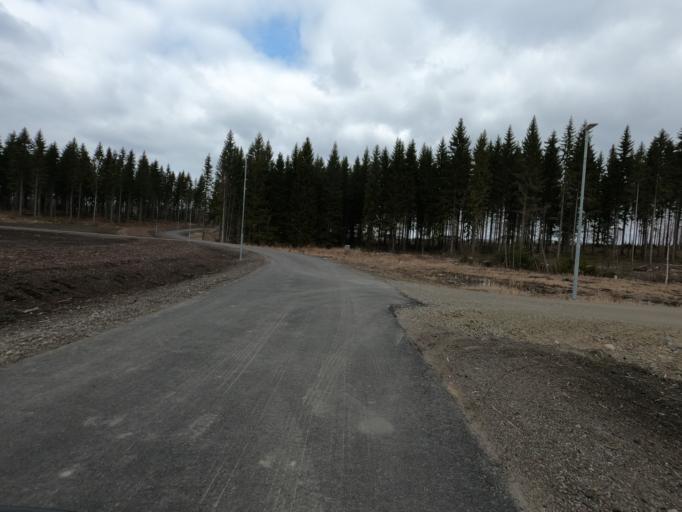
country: FI
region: North Karelia
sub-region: Joensuu
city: Joensuu
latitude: 62.5599
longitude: 29.8236
